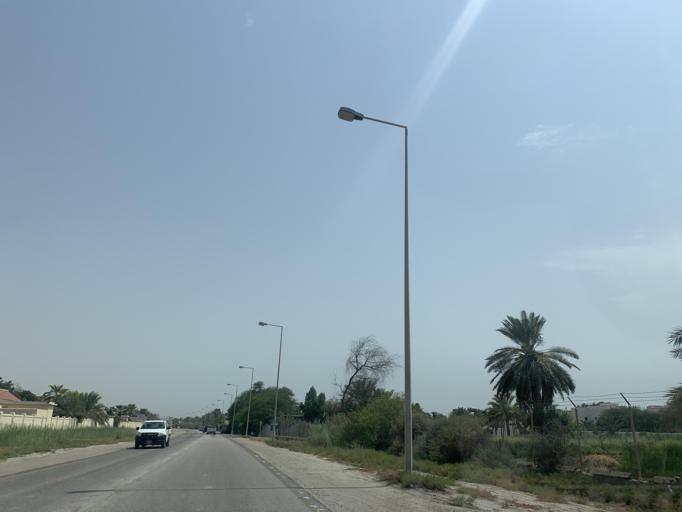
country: BH
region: Central Governorate
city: Madinat Hamad
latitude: 26.1664
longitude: 50.4652
